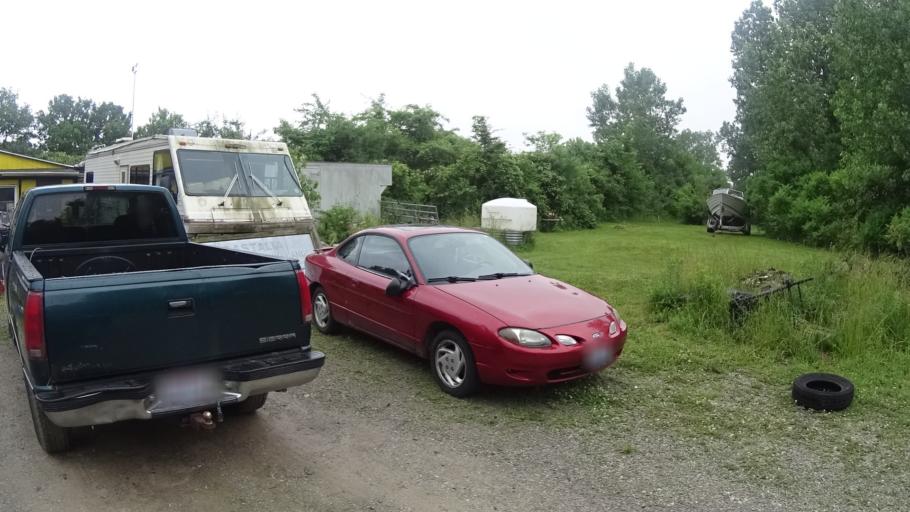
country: US
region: Ohio
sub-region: Huron County
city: Bellevue
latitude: 41.3489
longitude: -82.8191
